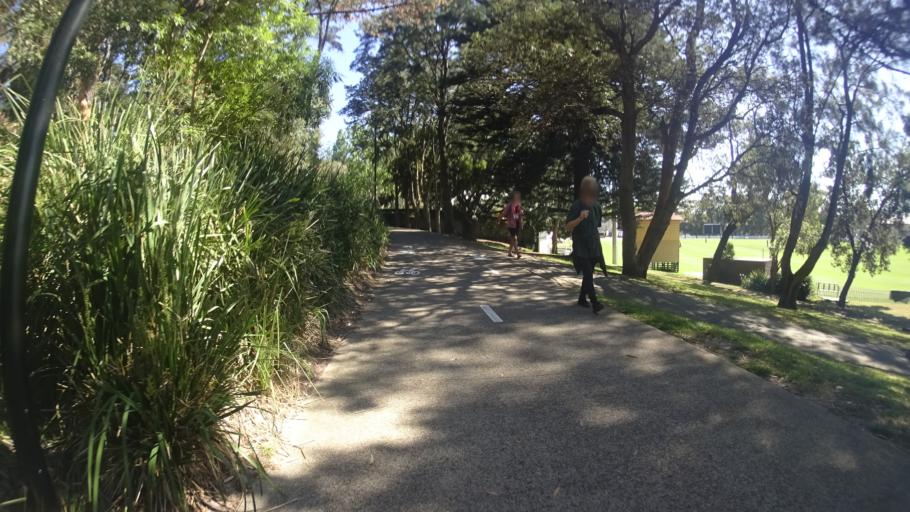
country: AU
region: New South Wales
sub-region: Waverley
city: Bondi
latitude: -33.8952
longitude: 151.2580
